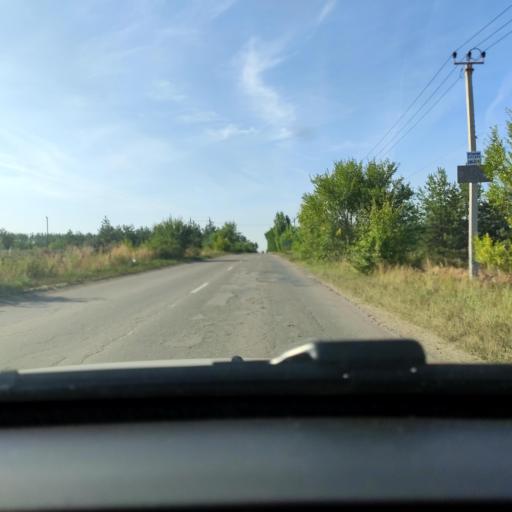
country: RU
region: Voronezj
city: Podgornoye
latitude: 51.8325
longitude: 39.2045
